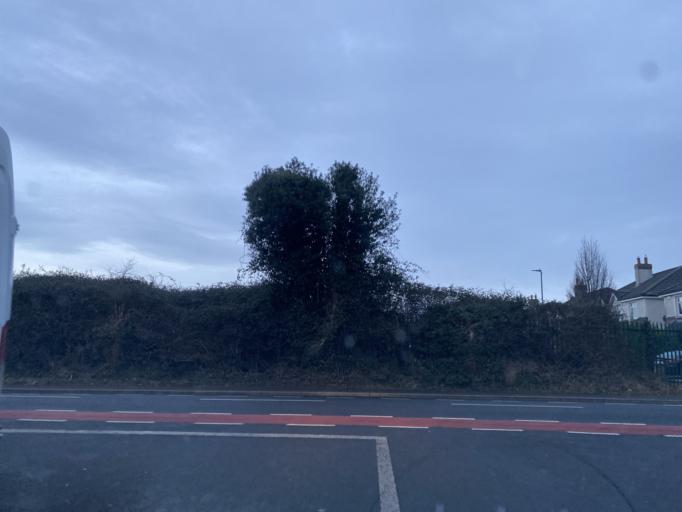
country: IE
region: Leinster
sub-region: Kildare
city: Celbridge
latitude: 53.3471
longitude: -6.5502
